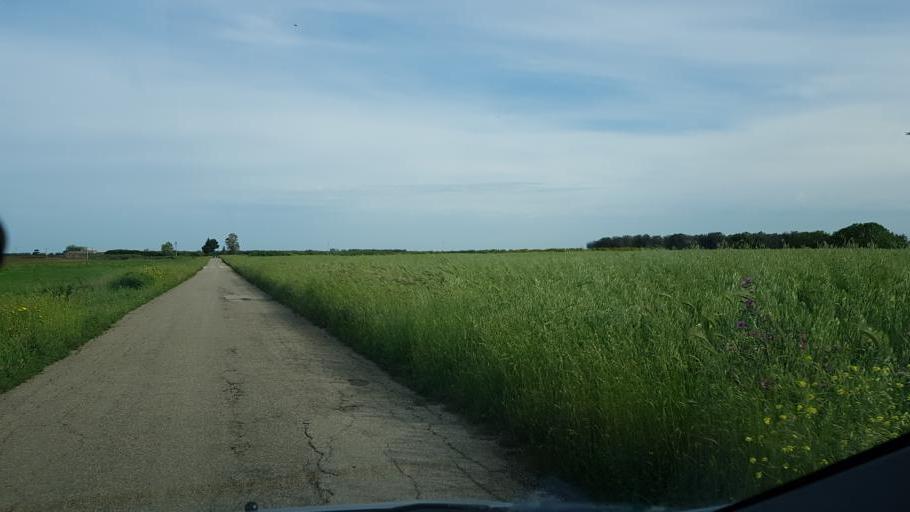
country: IT
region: Apulia
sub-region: Provincia di Brindisi
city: Tuturano
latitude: 40.5365
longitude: 17.9513
